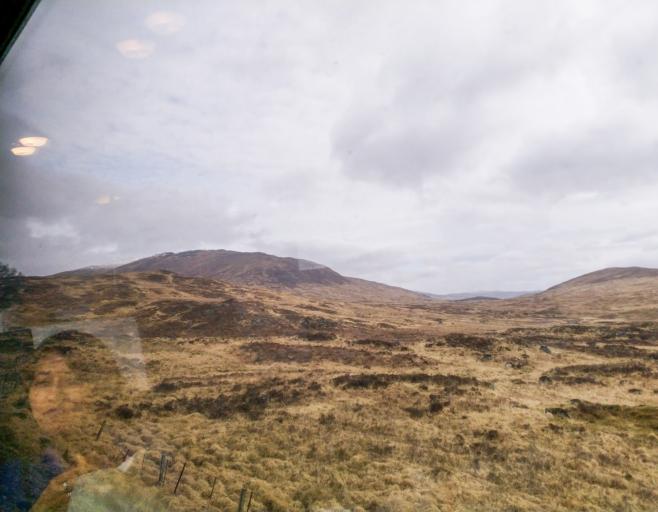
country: GB
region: Scotland
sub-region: Highland
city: Spean Bridge
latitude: 56.6990
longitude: -4.5758
